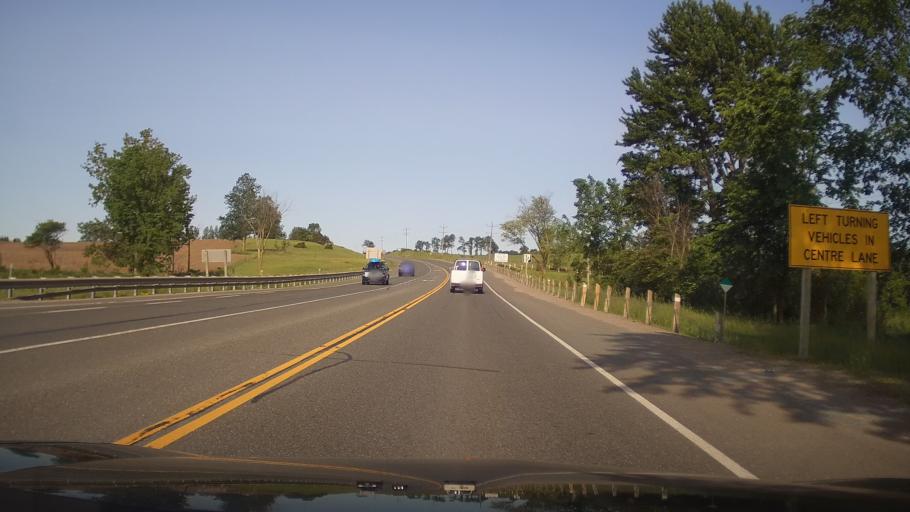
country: CA
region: Ontario
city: Peterborough
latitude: 44.3647
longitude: -78.0067
